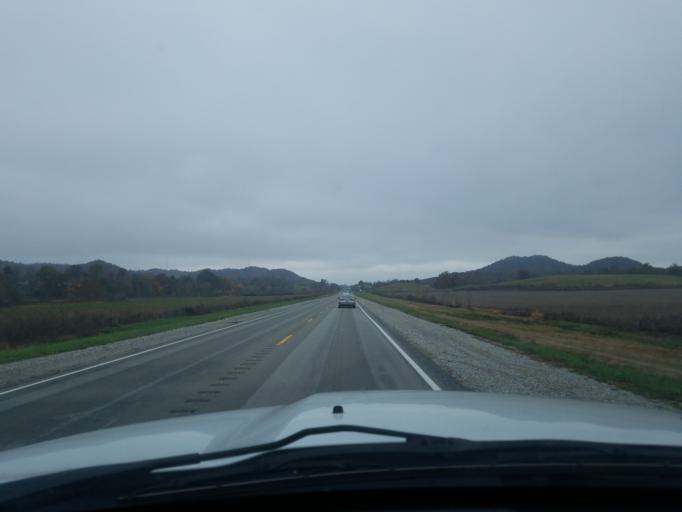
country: US
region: Kentucky
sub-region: Marion County
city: Lebanon
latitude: 37.5106
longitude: -85.2955
